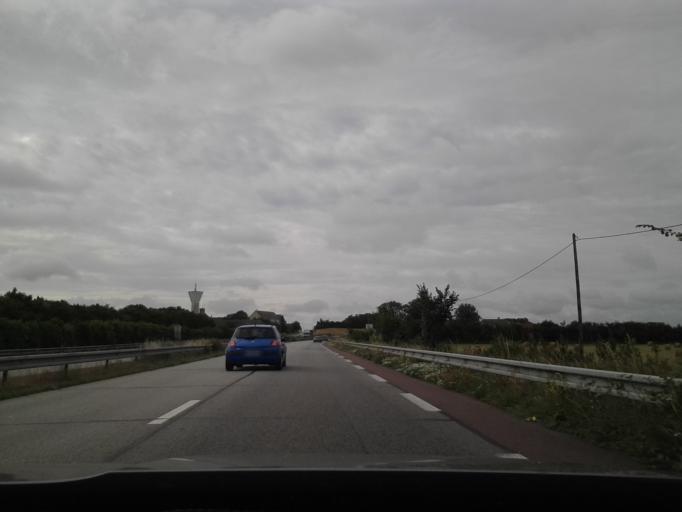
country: FR
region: Lower Normandy
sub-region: Departement de la Manche
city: Sainte-Mere-Eglise
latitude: 49.4167
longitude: -1.3240
